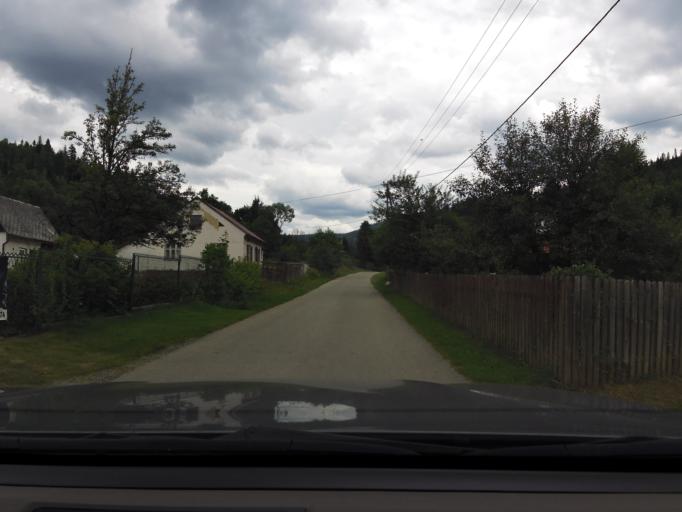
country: PL
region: Silesian Voivodeship
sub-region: Powiat zywiecki
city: Ujsoly
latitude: 49.5064
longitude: 19.1420
